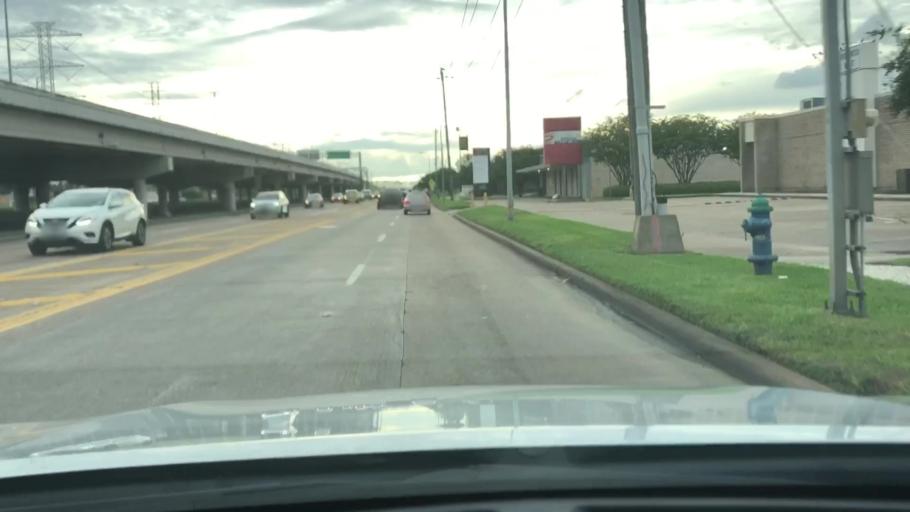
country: US
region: Texas
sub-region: Harris County
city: Piney Point Village
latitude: 29.7234
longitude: -95.4976
